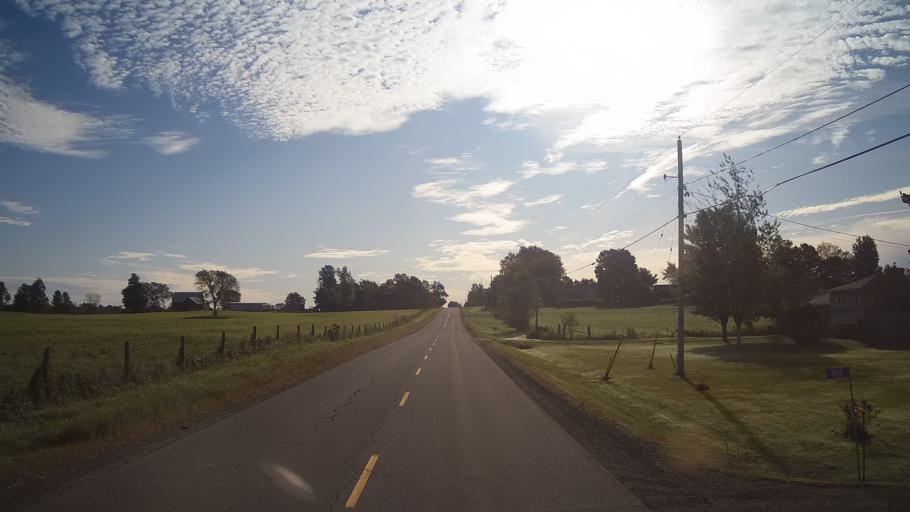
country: CA
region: Ontario
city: Gananoque
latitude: 44.4004
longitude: -76.0920
